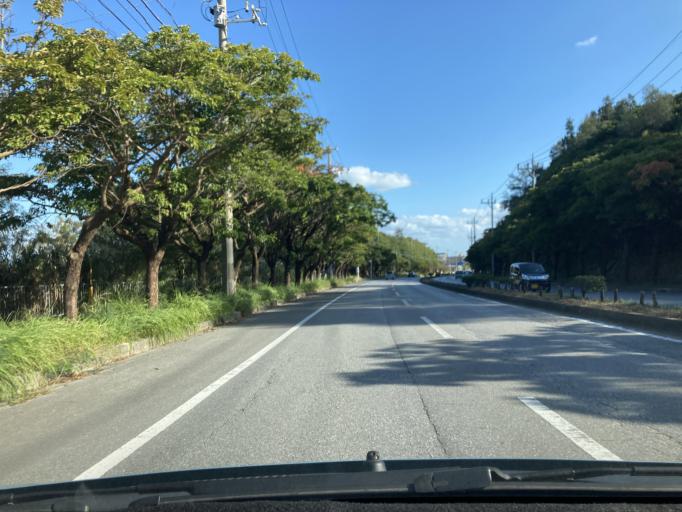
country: JP
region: Okinawa
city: Gushikawa
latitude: 26.3430
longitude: 127.8417
